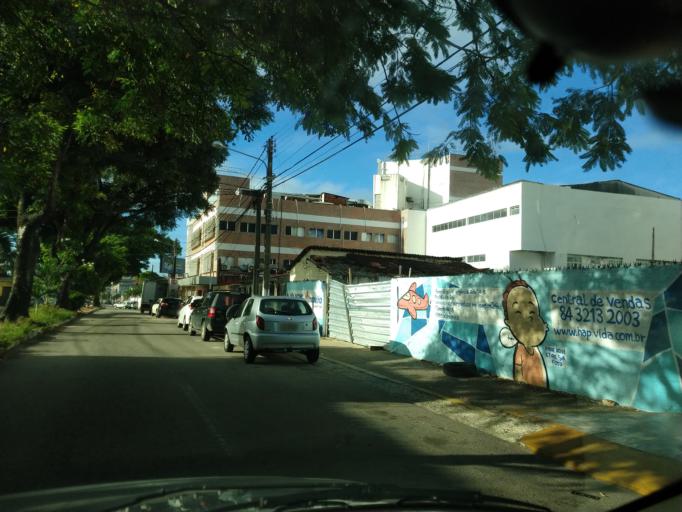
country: BR
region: Rio Grande do Norte
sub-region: Natal
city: Natal
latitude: -5.8043
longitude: -35.2130
